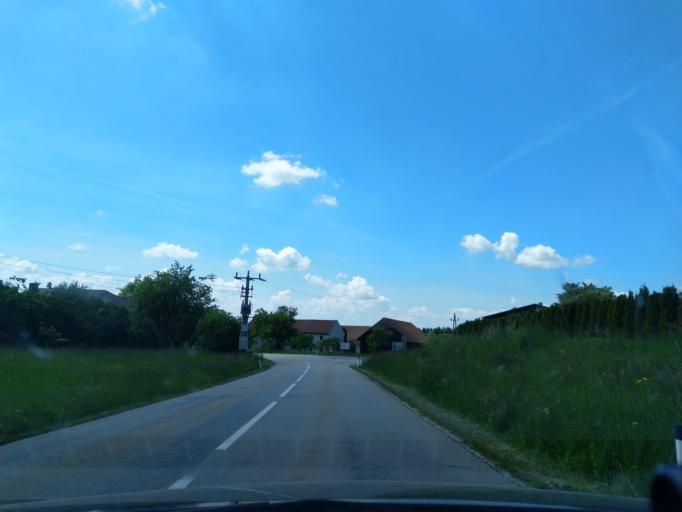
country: AT
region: Upper Austria
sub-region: Politischer Bezirk Ried im Innkreis
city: Ried im Innkreis
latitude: 48.2040
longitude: 13.5545
